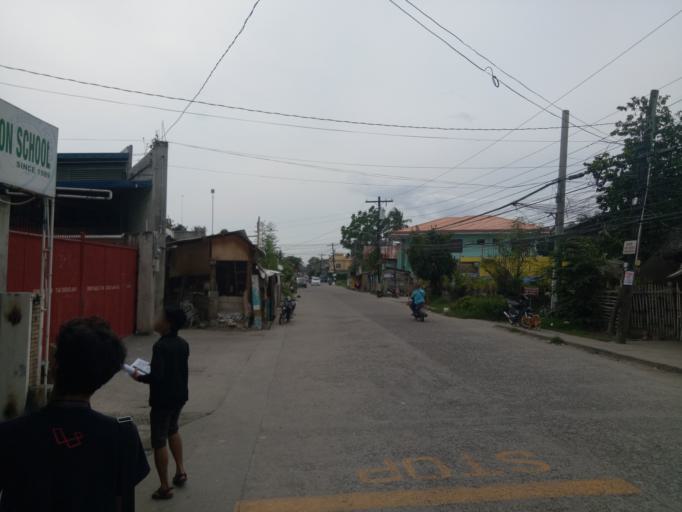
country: PH
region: Central Visayas
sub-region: Province of Negros Oriental
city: Dumaguete
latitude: 9.3044
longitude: 123.3014
